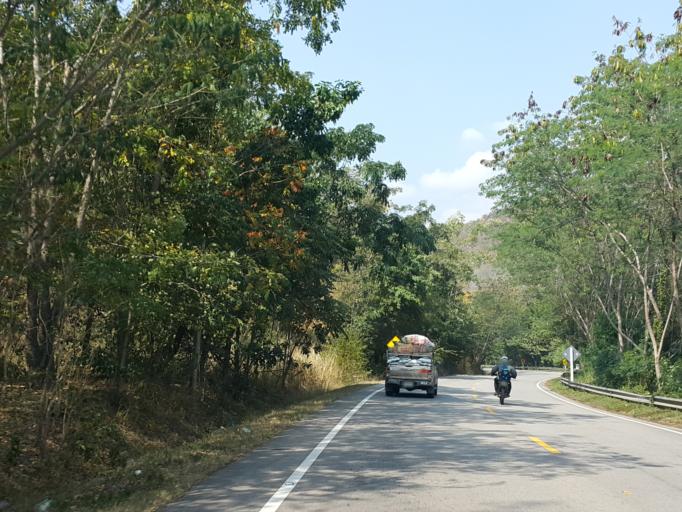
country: TH
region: Chiang Mai
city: Hot
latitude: 18.2315
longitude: 98.5567
